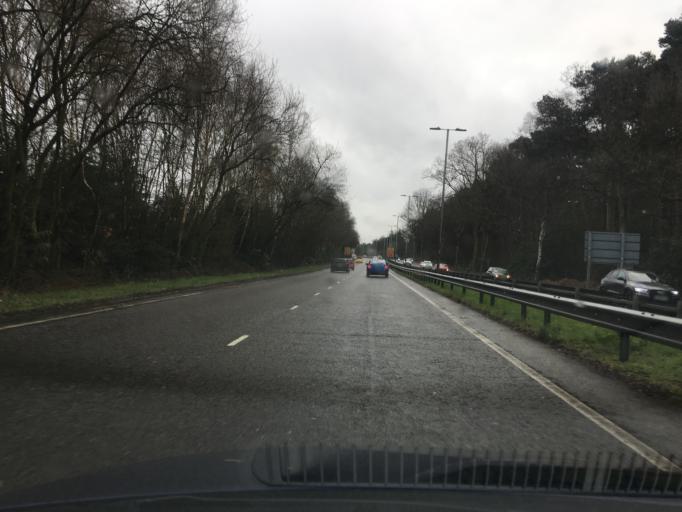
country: GB
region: England
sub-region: Bracknell Forest
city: Crowthorne
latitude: 51.3861
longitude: -0.7724
